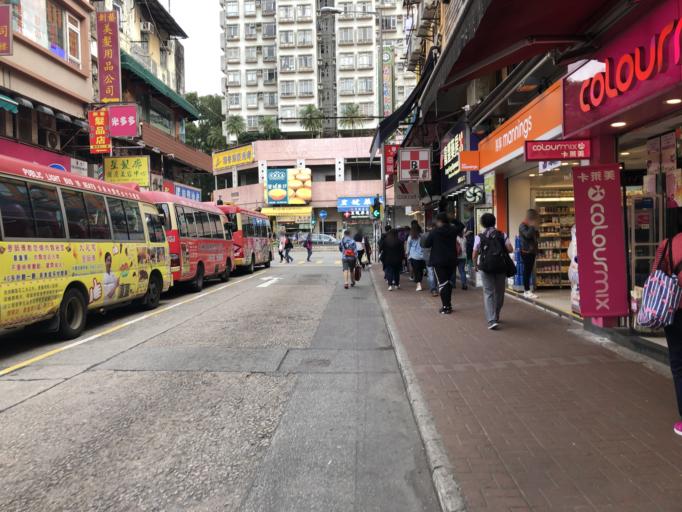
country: HK
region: Tai Po
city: Tai Po
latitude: 22.5037
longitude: 114.1293
